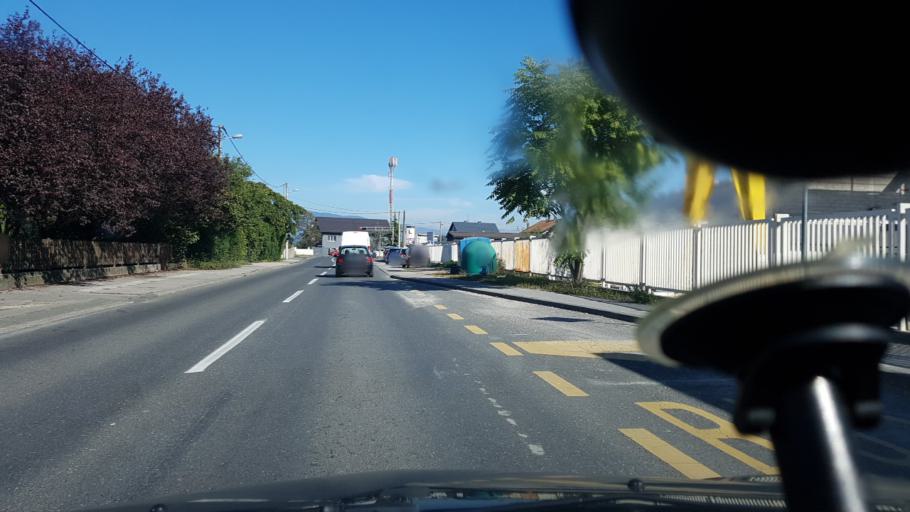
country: HR
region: Grad Zagreb
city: Lucko
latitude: 45.7588
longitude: 15.8929
